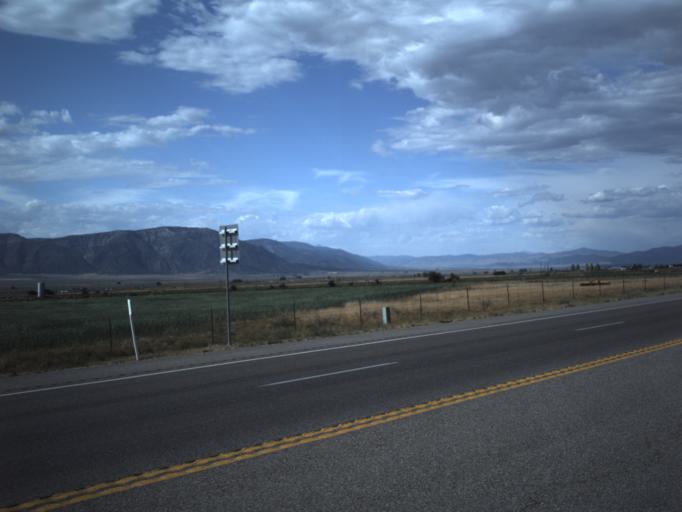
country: US
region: Utah
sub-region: Sanpete County
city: Ephraim
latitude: 39.3236
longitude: -111.6042
